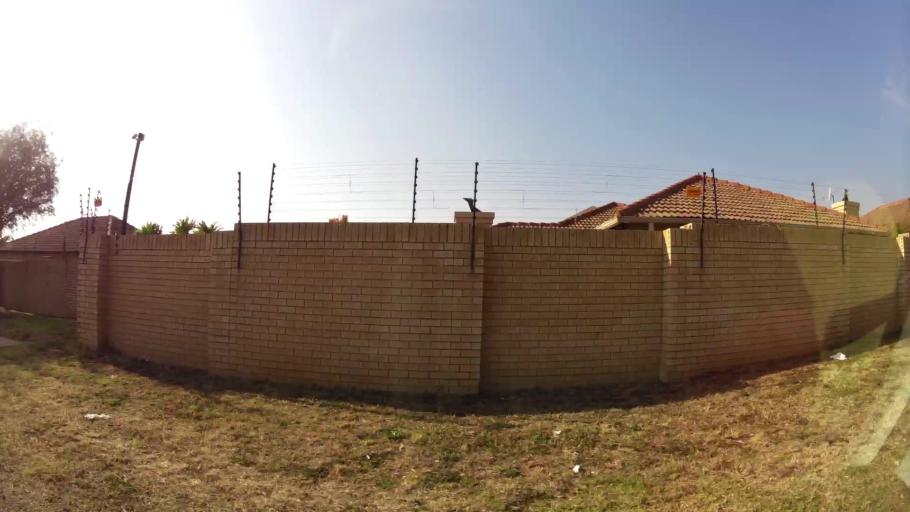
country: ZA
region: Gauteng
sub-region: City of Tshwane Metropolitan Municipality
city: Pretoria
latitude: -25.7537
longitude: 28.3266
